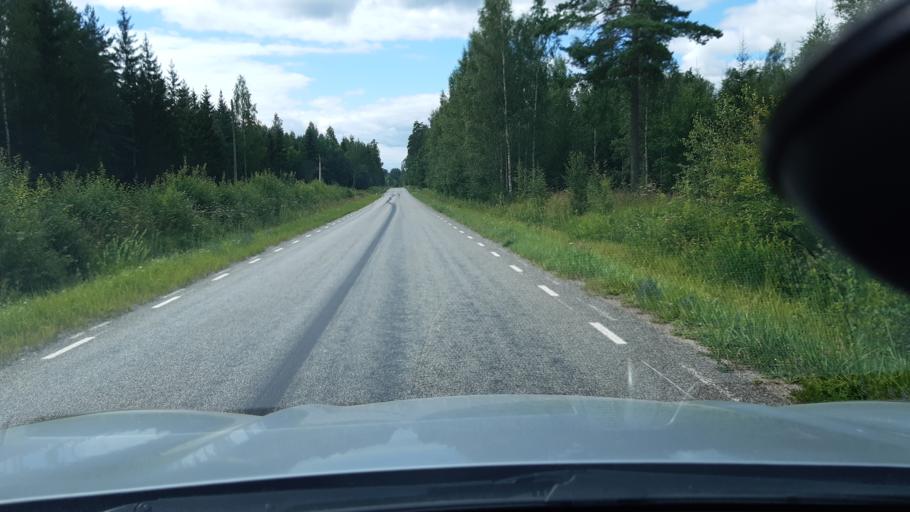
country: EE
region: Raplamaa
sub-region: Jaervakandi vald
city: Jarvakandi
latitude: 58.7935
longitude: 24.8543
